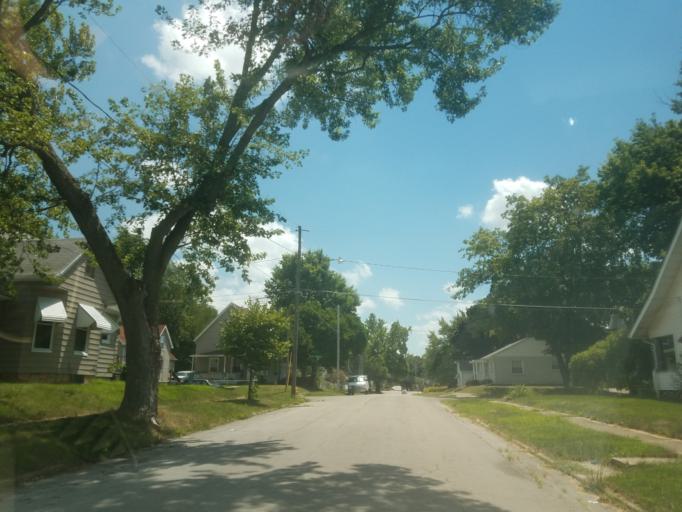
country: US
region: Illinois
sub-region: McLean County
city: Bloomington
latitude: 40.4745
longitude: -89.0100
